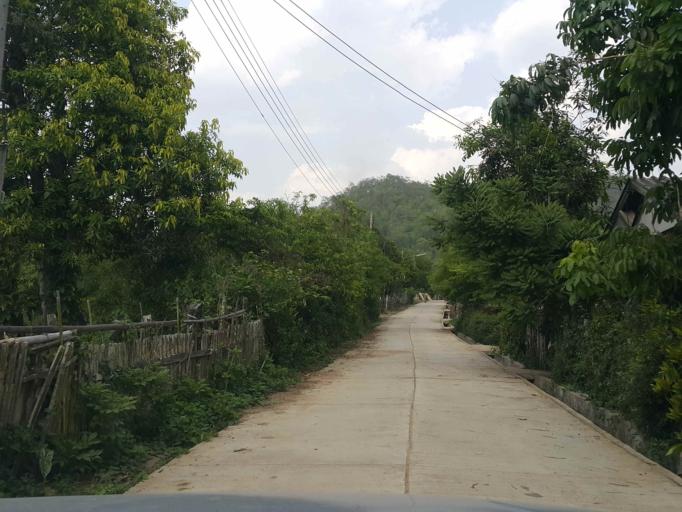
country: TH
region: Chiang Mai
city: Wiang Haeng
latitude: 19.3971
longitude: 98.7199
